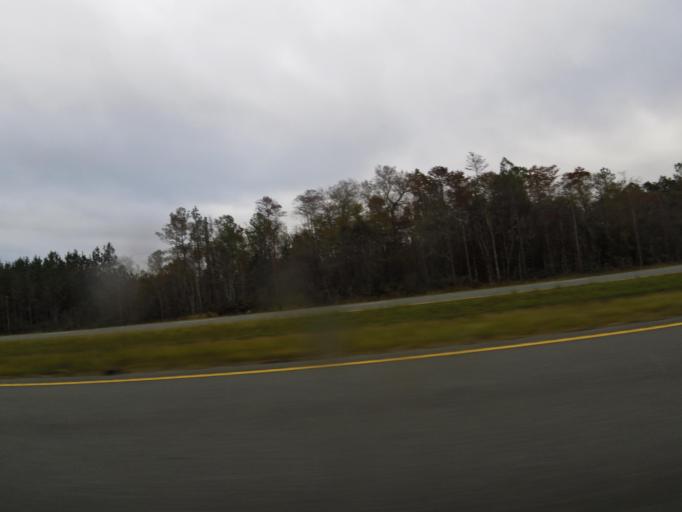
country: US
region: Georgia
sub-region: Charlton County
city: Folkston
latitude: 30.8969
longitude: -82.0573
